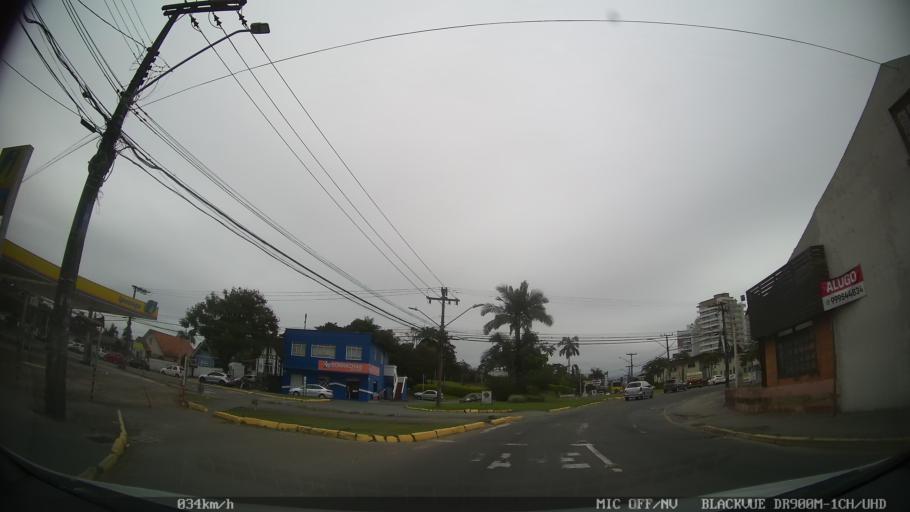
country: BR
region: Santa Catarina
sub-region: Joinville
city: Joinville
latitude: -26.2831
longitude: -48.8407
